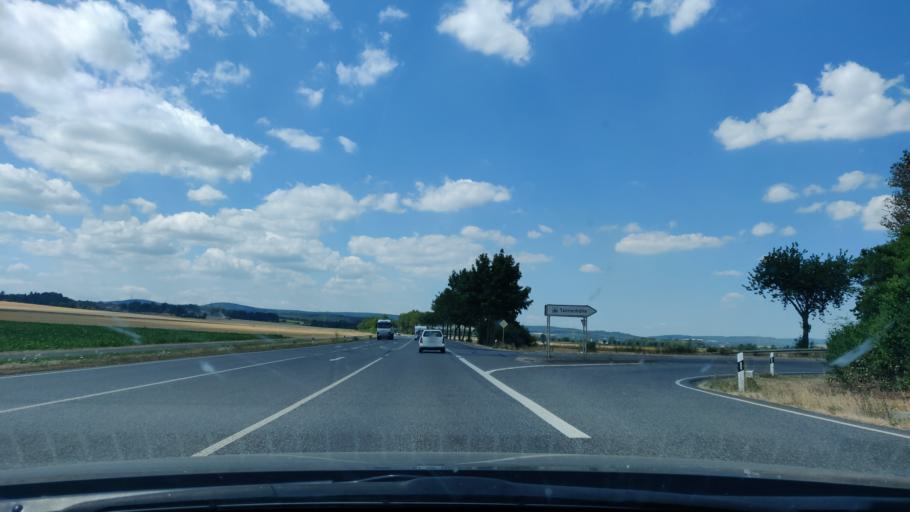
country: DE
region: Hesse
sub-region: Regierungsbezirk Kassel
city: Wabern
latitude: 51.0949
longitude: 9.3261
